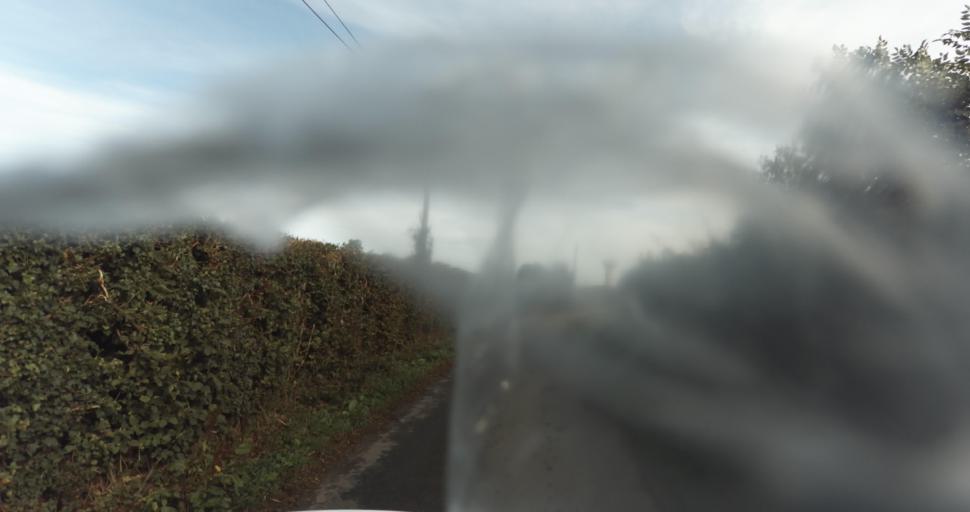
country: FR
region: Lower Normandy
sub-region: Departement de l'Orne
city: Gace
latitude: 48.8989
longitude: 0.3138
